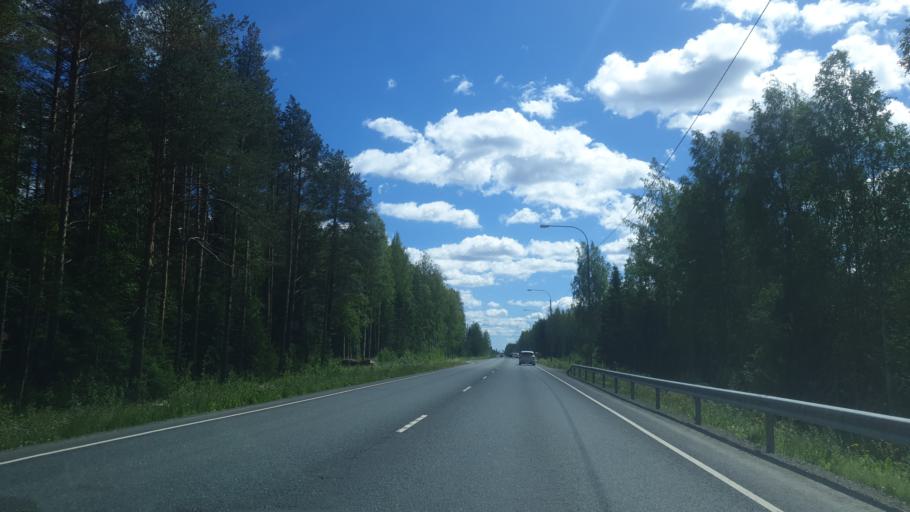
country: FI
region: Northern Savo
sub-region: Varkaus
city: Leppaevirta
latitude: 62.5231
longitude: 27.6729
